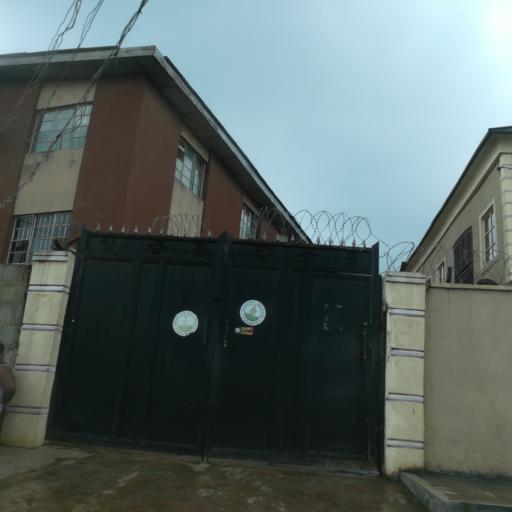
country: NG
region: Lagos
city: Agege
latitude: 6.5945
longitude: 3.2976
